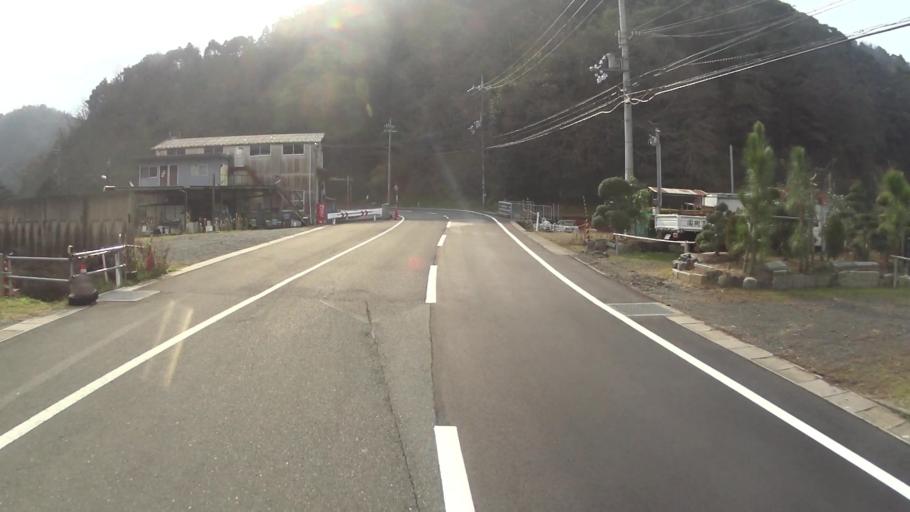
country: JP
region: Kyoto
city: Maizuru
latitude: 35.4794
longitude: 135.3165
